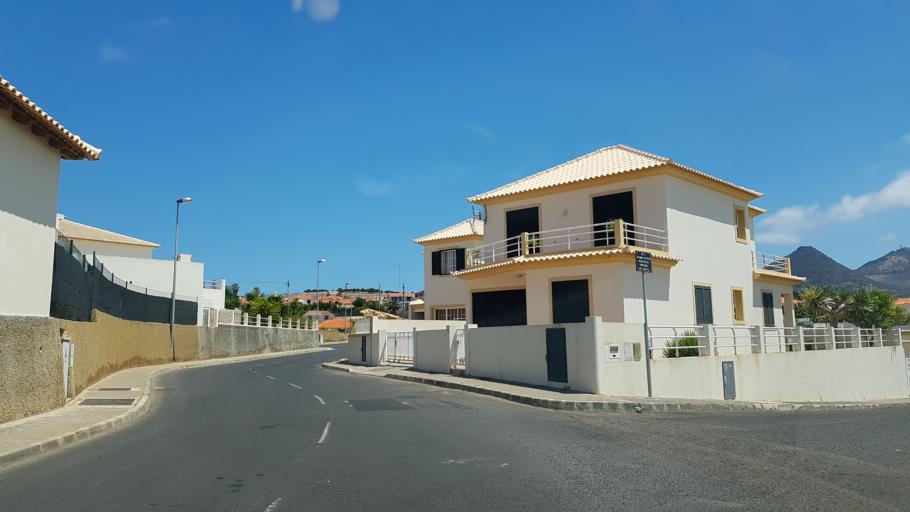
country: PT
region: Madeira
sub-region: Porto Santo
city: Vila de Porto Santo
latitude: 33.0559
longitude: -16.3564
